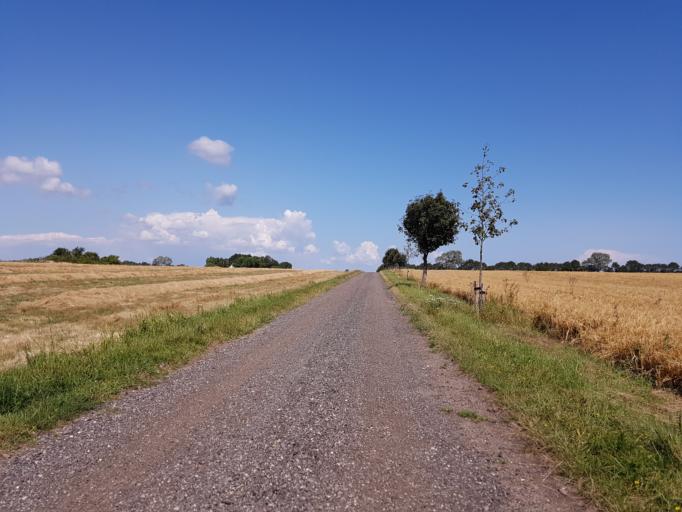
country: DK
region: Zealand
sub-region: Guldborgsund Kommune
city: Nykobing Falster
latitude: 54.5699
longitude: 11.9518
